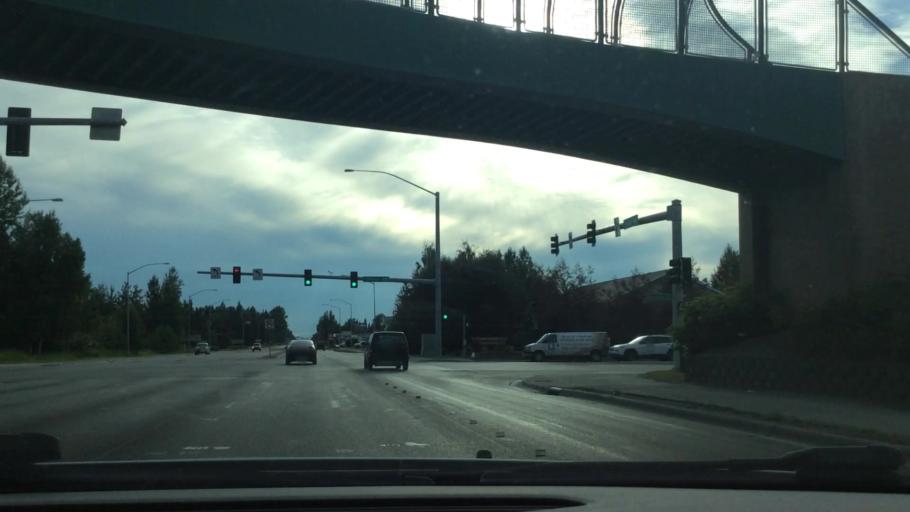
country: US
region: Alaska
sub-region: Anchorage Municipality
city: Anchorage
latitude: 61.1809
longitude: -149.8072
